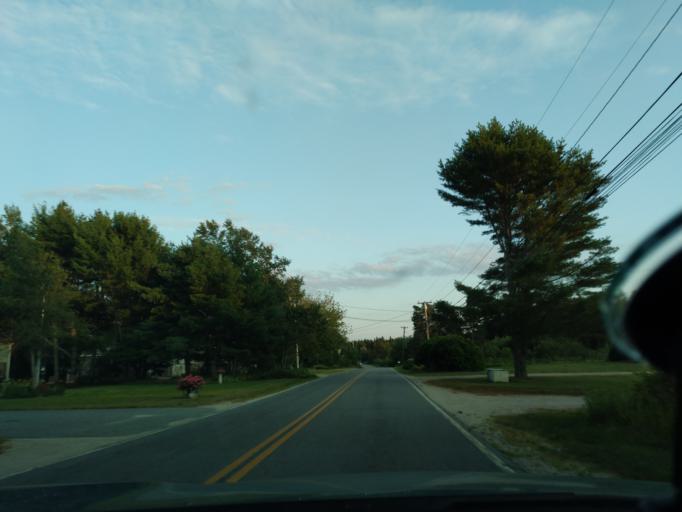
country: US
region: Maine
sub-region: Hancock County
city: Gouldsboro
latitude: 44.3753
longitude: -68.0353
